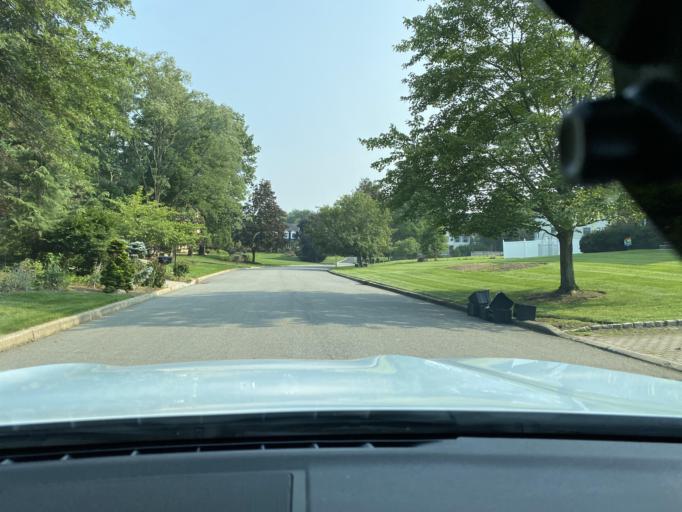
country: US
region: New York
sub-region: Rockland County
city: Airmont
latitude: 41.0896
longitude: -74.1230
